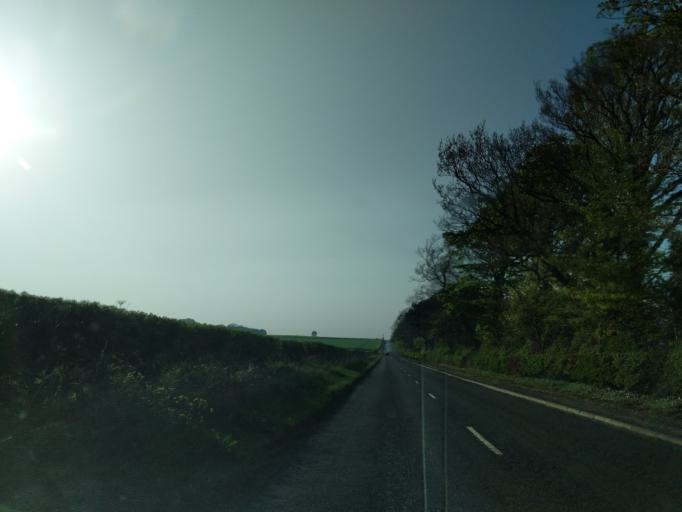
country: GB
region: Scotland
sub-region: Fife
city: Pathhead
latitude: 55.8788
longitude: -3.0115
